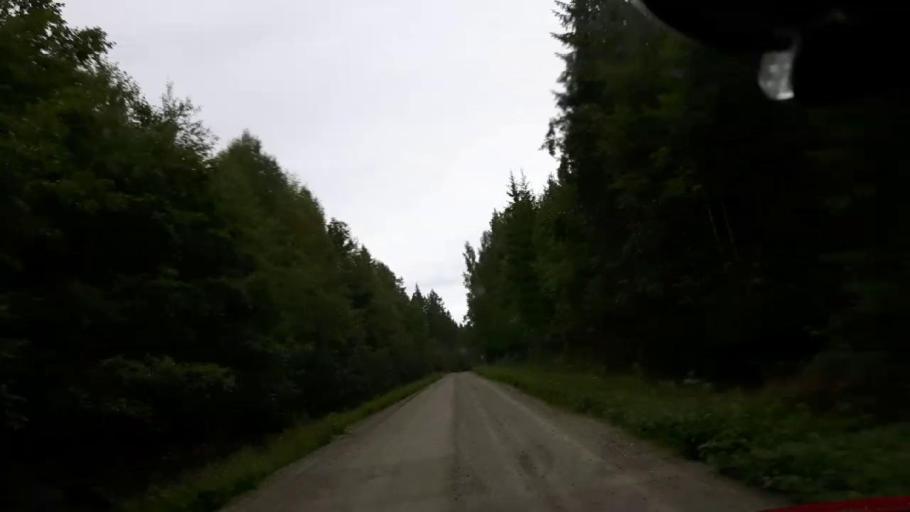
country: SE
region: Vaesternorrland
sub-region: Ange Kommun
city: Ange
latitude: 62.7958
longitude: 15.7714
